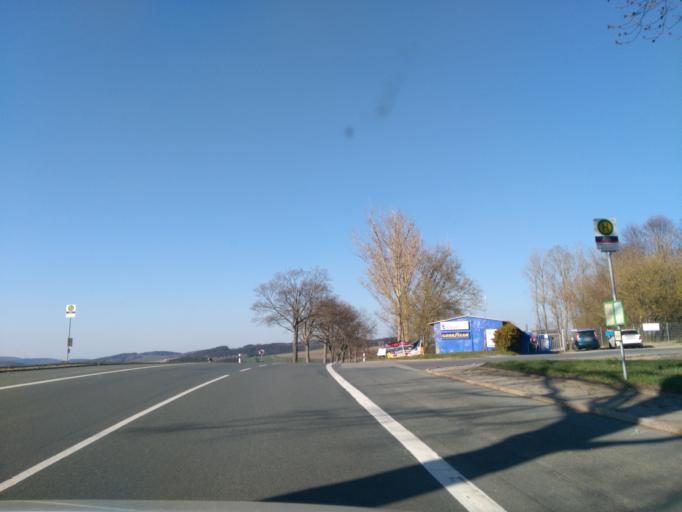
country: DE
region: Saxony
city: Schlettau
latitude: 50.5512
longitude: 12.9429
